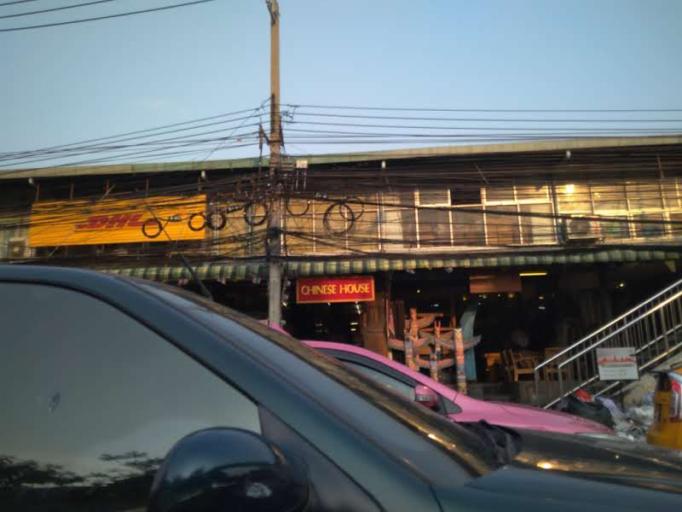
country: TH
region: Bangkok
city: Bang Sue
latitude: 13.8006
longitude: 100.5484
